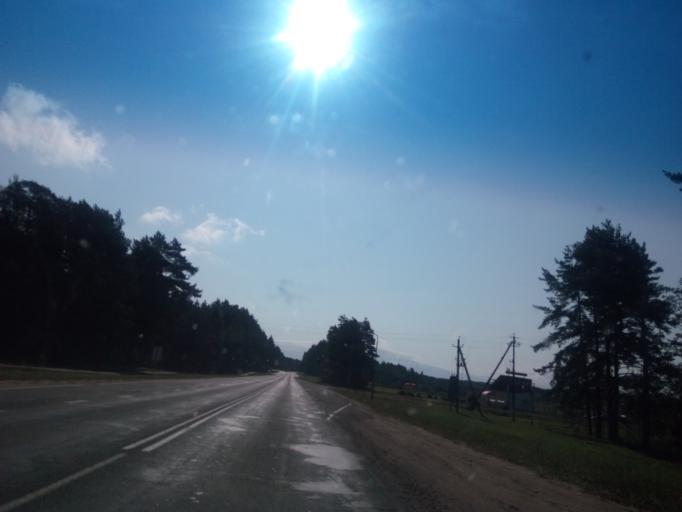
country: BY
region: Vitebsk
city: Vyerkhnyadzvinsk
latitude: 55.7576
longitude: 27.9515
